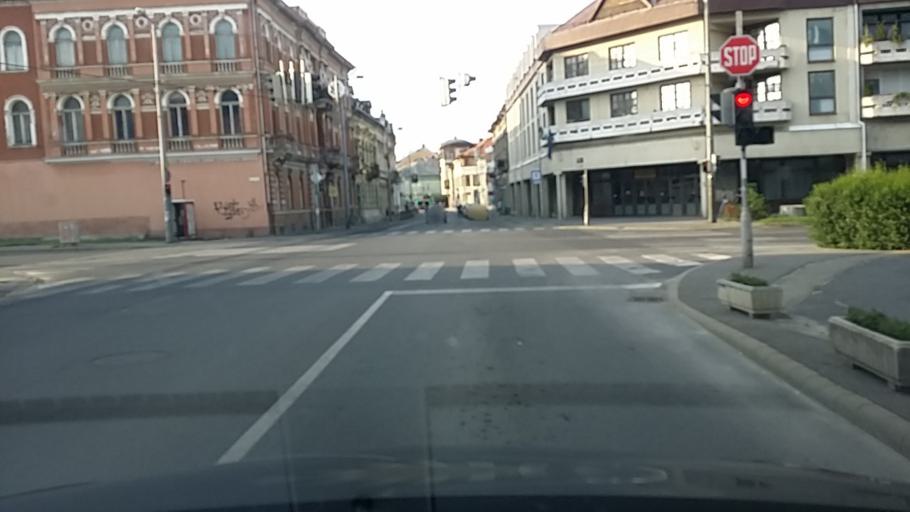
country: HU
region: Borsod-Abauj-Zemplen
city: Miskolc
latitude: 48.1006
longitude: 20.7853
